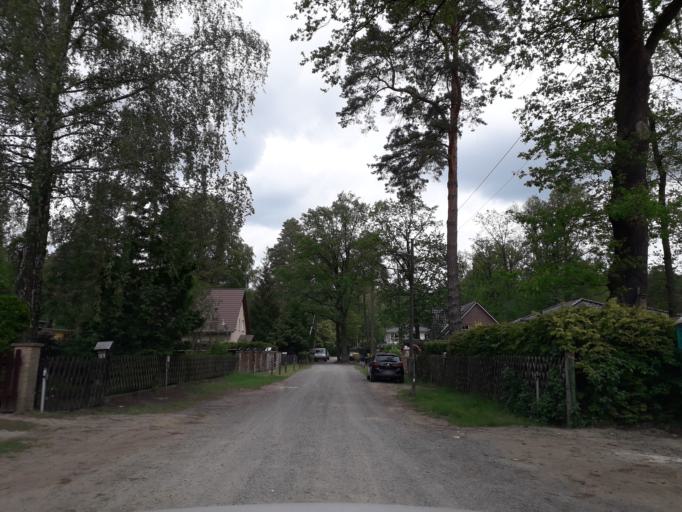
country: DE
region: Brandenburg
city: Falkensee
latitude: 52.5885
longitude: 13.0738
